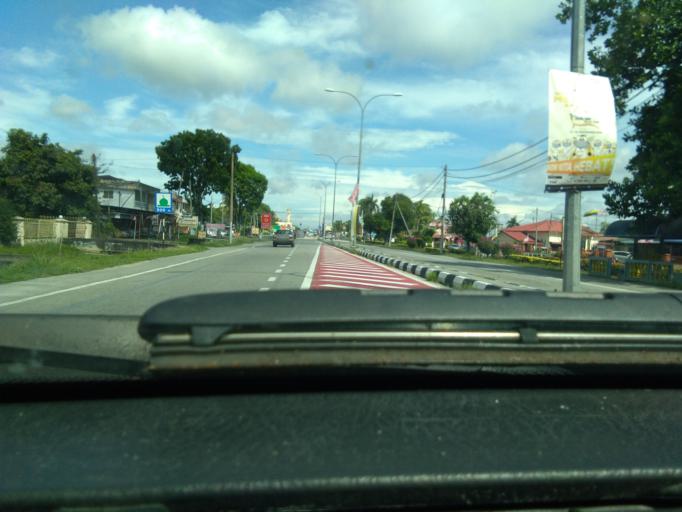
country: MY
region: Perak
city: Bagan Serai
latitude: 5.0074
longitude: 100.5411
